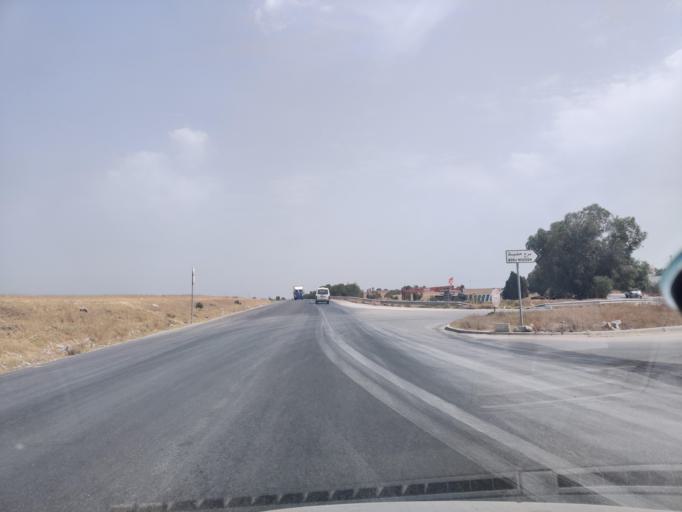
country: TN
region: Nabul
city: Bu `Urqub
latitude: 36.4658
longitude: 10.5718
